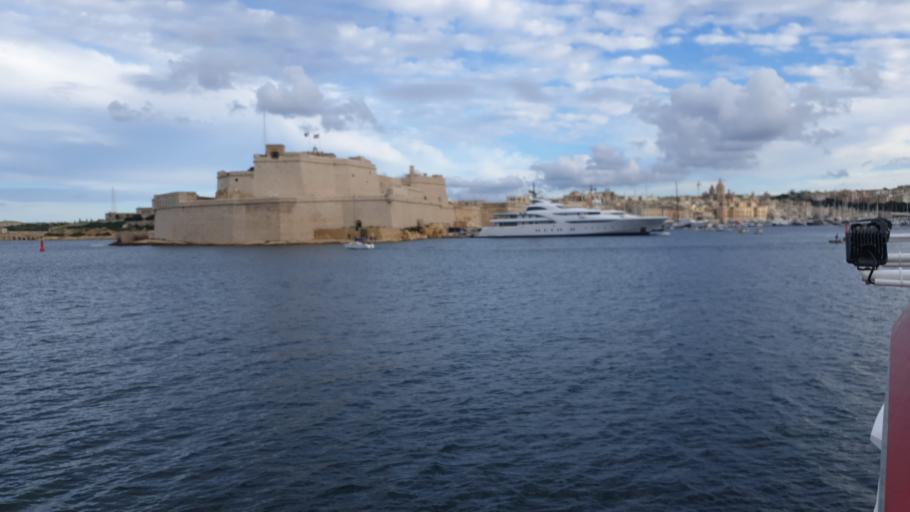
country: MT
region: Il-Birgu
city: Vittoriosa
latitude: 35.8929
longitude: 14.5140
